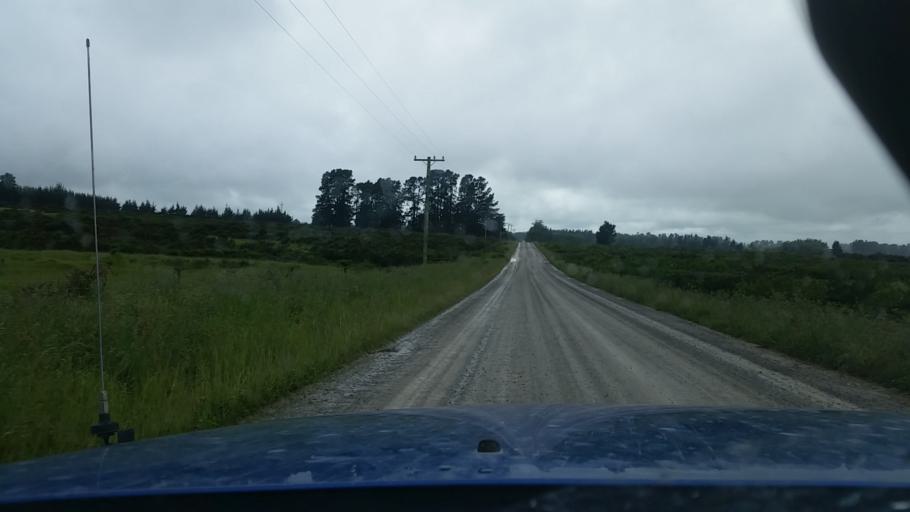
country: NZ
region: Canterbury
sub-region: Ashburton District
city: Methven
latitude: -43.6071
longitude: 171.4697
